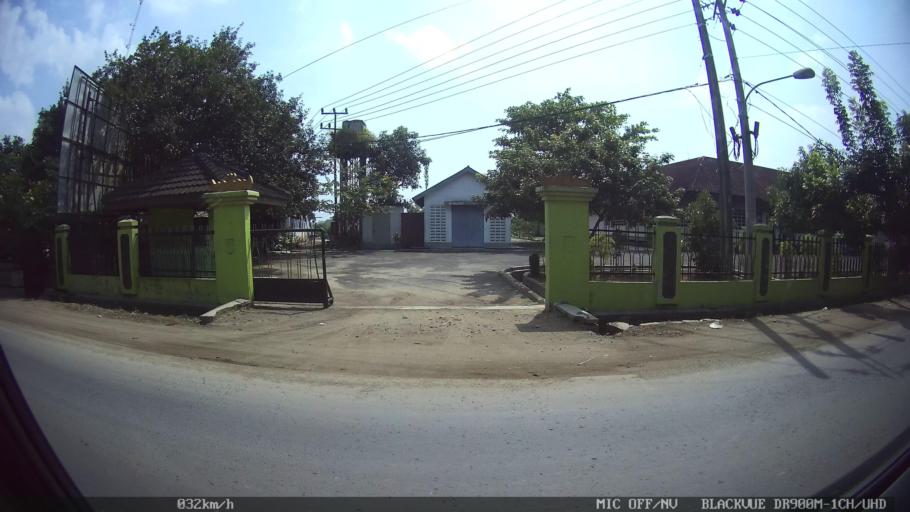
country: ID
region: Lampung
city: Pringsewu
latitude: -5.3729
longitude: 105.0125
